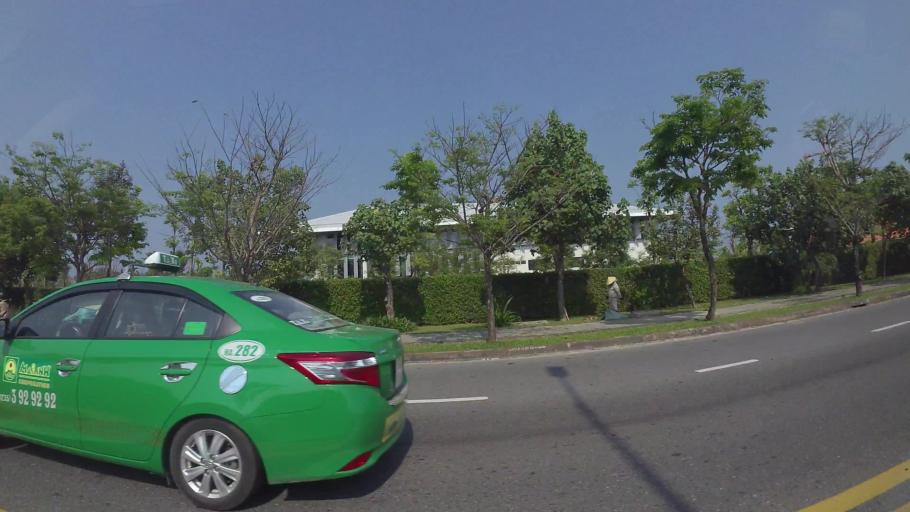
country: VN
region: Da Nang
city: Ngu Hanh Son
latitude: 16.0337
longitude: 108.2524
